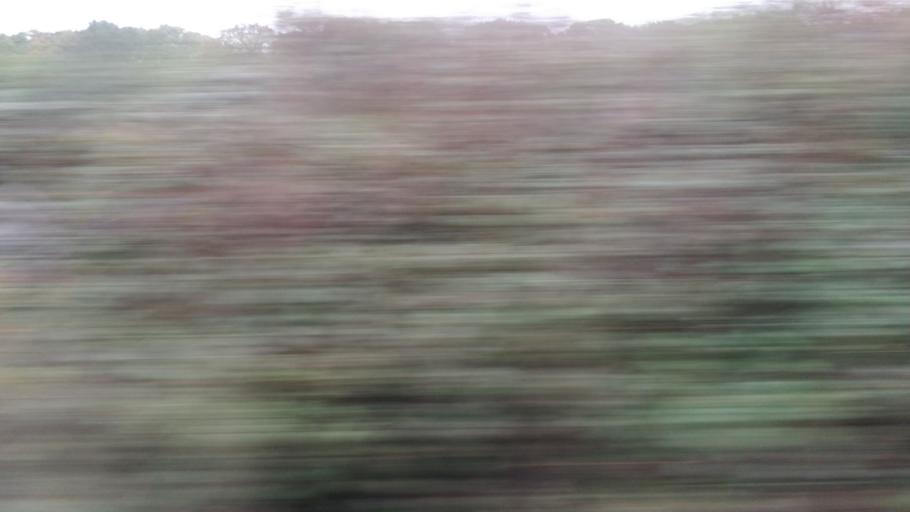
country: GB
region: England
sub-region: Lancashire
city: Parbold
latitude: 53.5872
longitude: -2.7564
